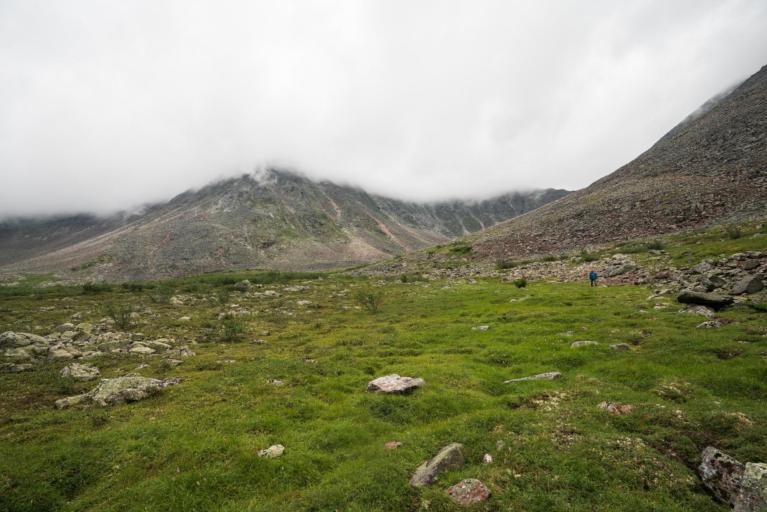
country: RU
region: Transbaikal Territory
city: Kuanda
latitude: 56.7593
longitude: 116.5509
